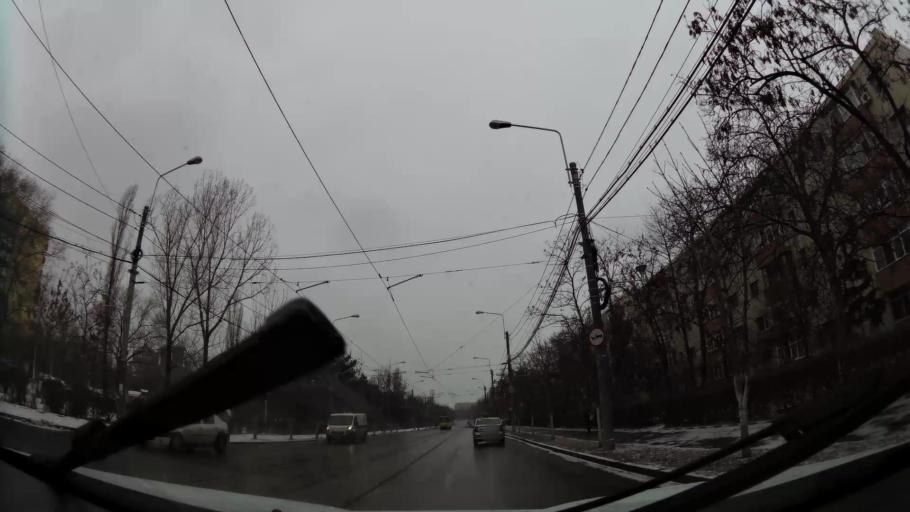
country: RO
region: Prahova
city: Ploiesti
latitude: 44.9582
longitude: 26.0109
